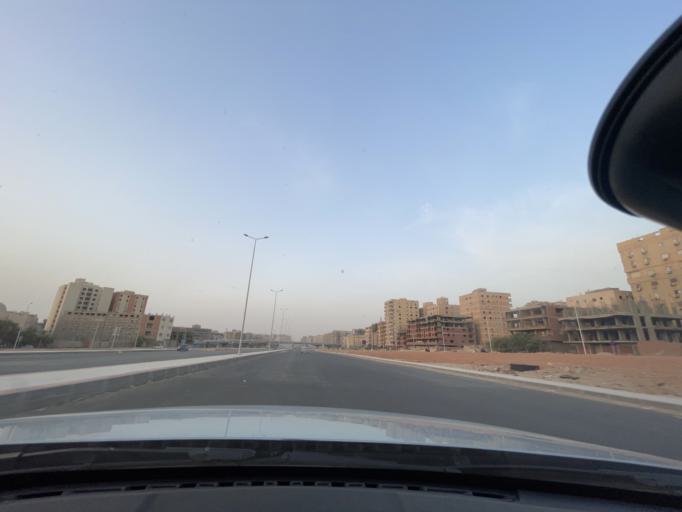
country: EG
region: Muhafazat al Qahirah
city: Cairo
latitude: 30.0548
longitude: 31.3726
